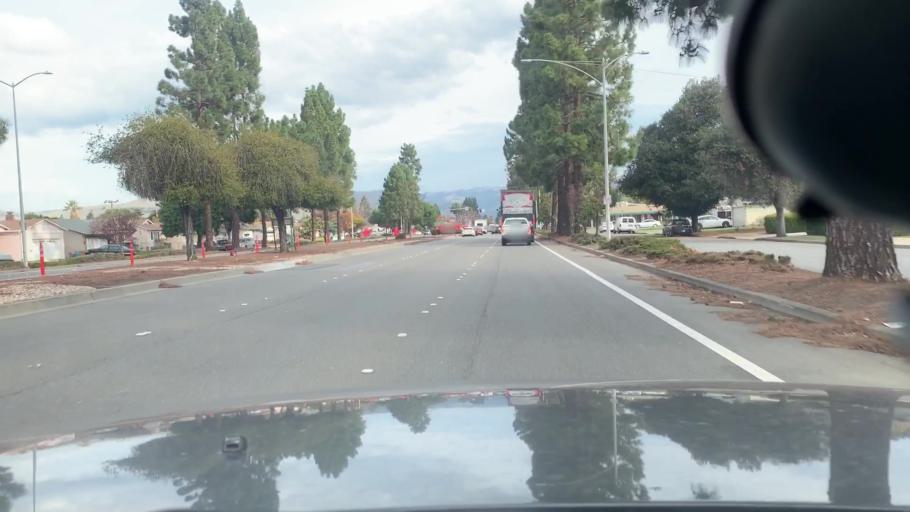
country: US
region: California
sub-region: Alameda County
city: Fremont
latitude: 37.5435
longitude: -121.9924
